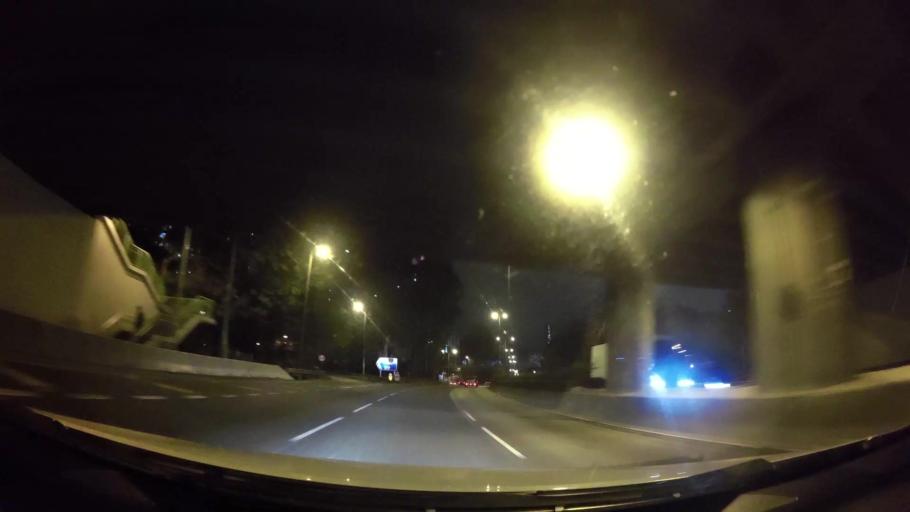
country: HK
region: Wong Tai Sin
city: Wong Tai Sin
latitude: 22.3417
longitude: 114.1986
